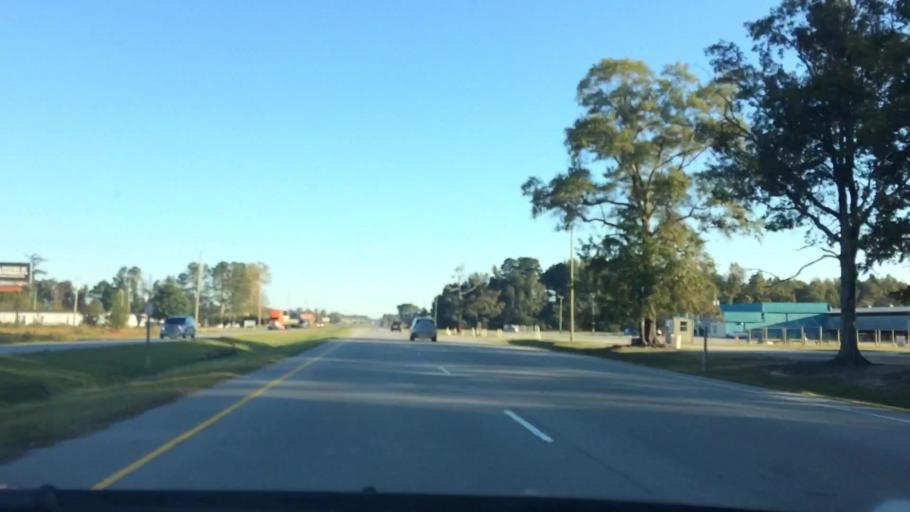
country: US
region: North Carolina
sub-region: Pitt County
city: Grifton
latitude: 35.4223
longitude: -77.4340
